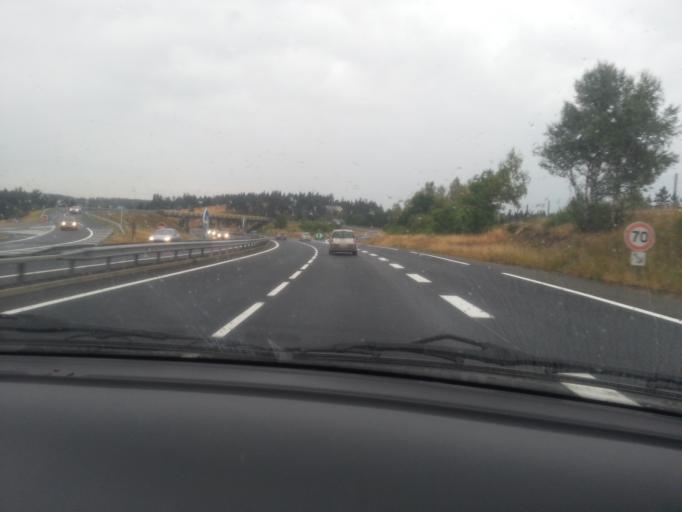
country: FR
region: Languedoc-Roussillon
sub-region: Departement de la Lozere
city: Aumont-Aubrac
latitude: 44.6983
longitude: 3.2827
